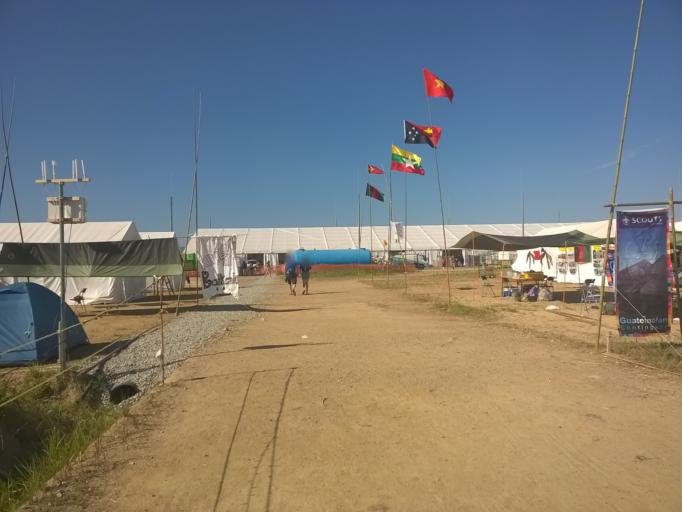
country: JP
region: Yamaguchi
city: Ogori-shimogo
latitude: 34.0138
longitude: 131.3726
